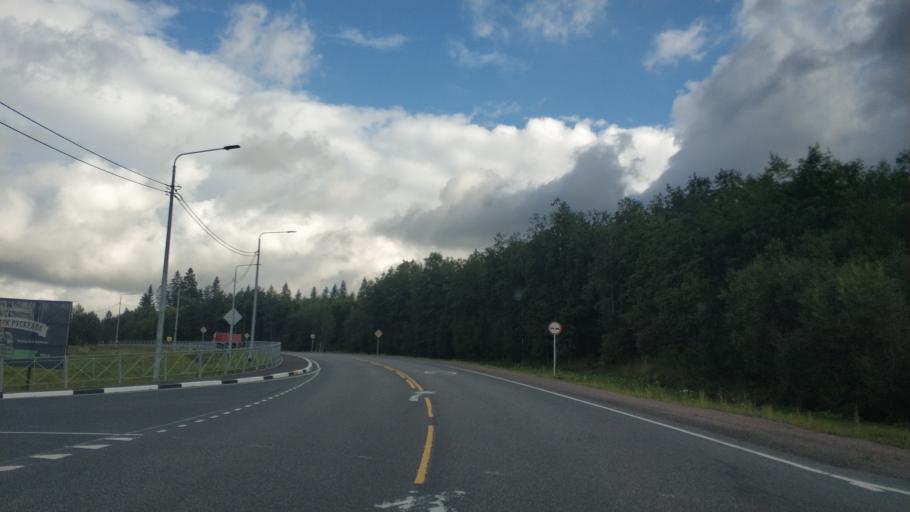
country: RU
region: Republic of Karelia
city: Ruskeala
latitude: 61.9461
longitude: 30.5988
